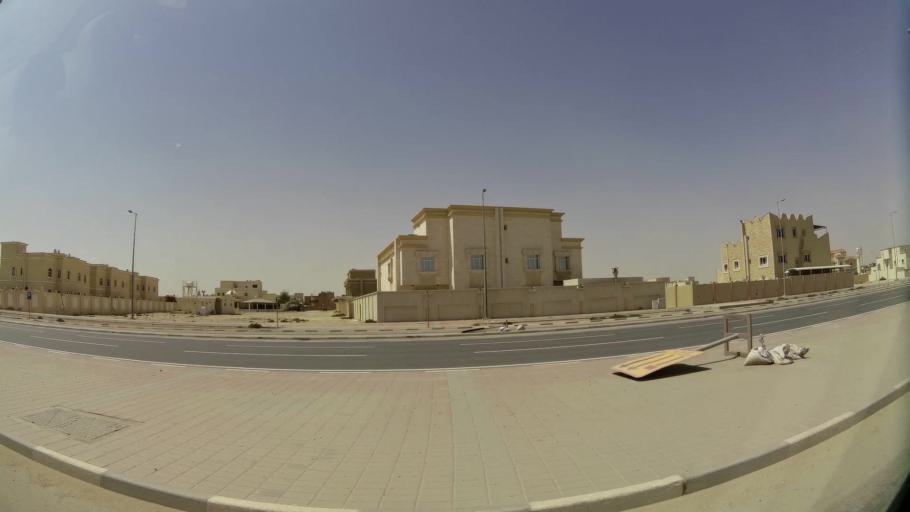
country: QA
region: Baladiyat Umm Salal
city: Umm Salal Muhammad
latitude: 25.3862
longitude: 51.4667
